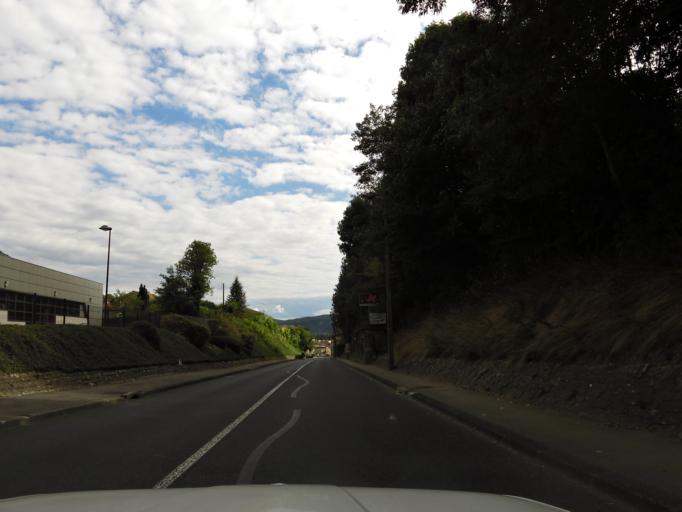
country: FR
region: Rhone-Alpes
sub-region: Departement de l'Ain
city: Lagnieu
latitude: 45.9079
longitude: 5.3470
